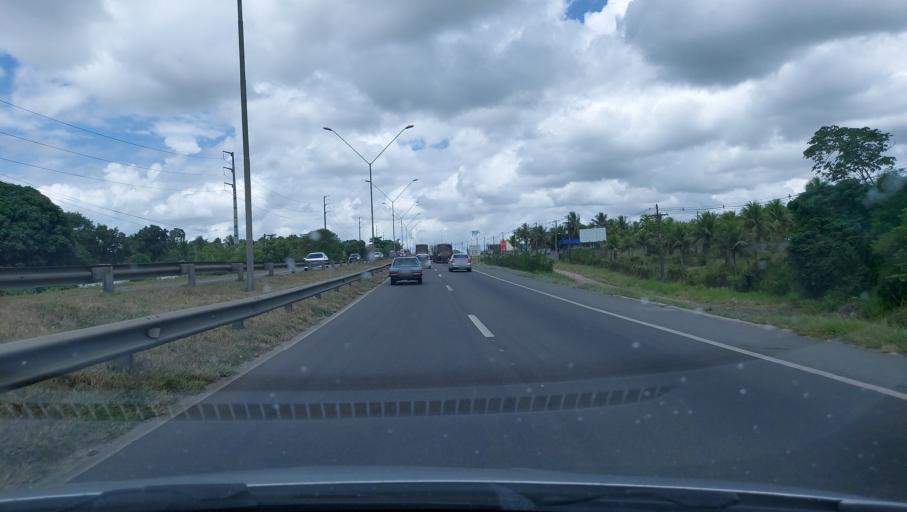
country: BR
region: Bahia
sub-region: Conceicao Do Jacuipe
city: Conceicao do Jacuipe
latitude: -12.3238
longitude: -38.8673
